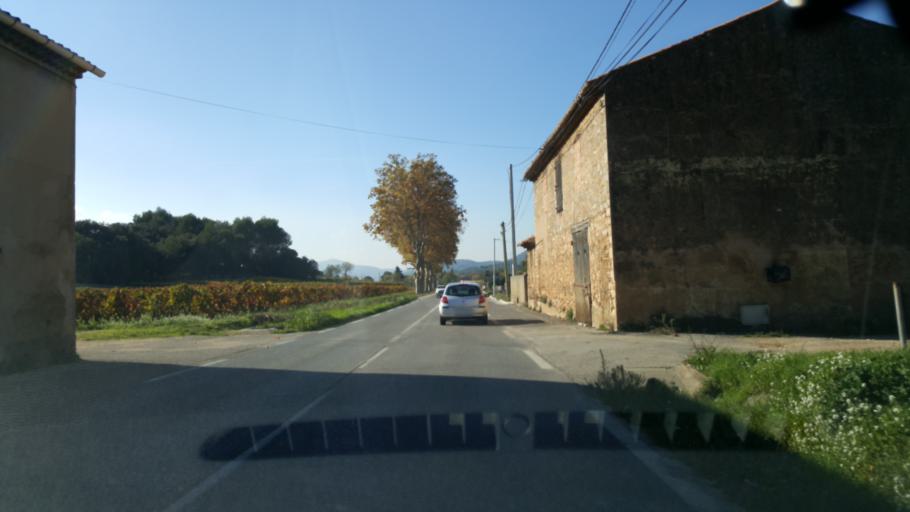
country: FR
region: Provence-Alpes-Cote d'Azur
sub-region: Departement du Var
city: Saint-Zacharie
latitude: 43.3774
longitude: 5.6842
